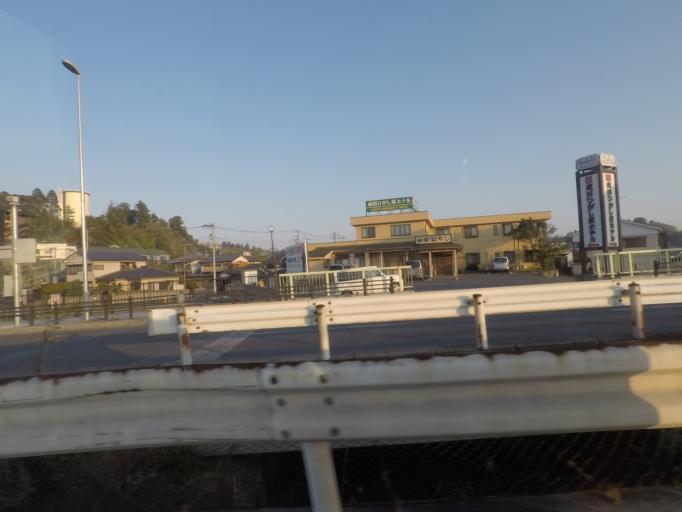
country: JP
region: Chiba
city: Narita
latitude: 35.7806
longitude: 140.3244
